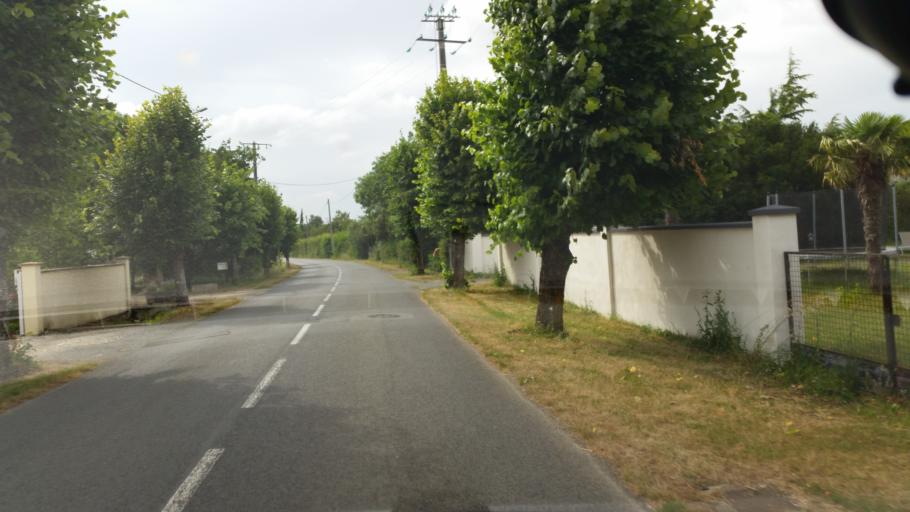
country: FR
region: Poitou-Charentes
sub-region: Departement de la Charente-Maritime
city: Saint-Jean-de-Liversay
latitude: 46.2131
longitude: -0.8780
